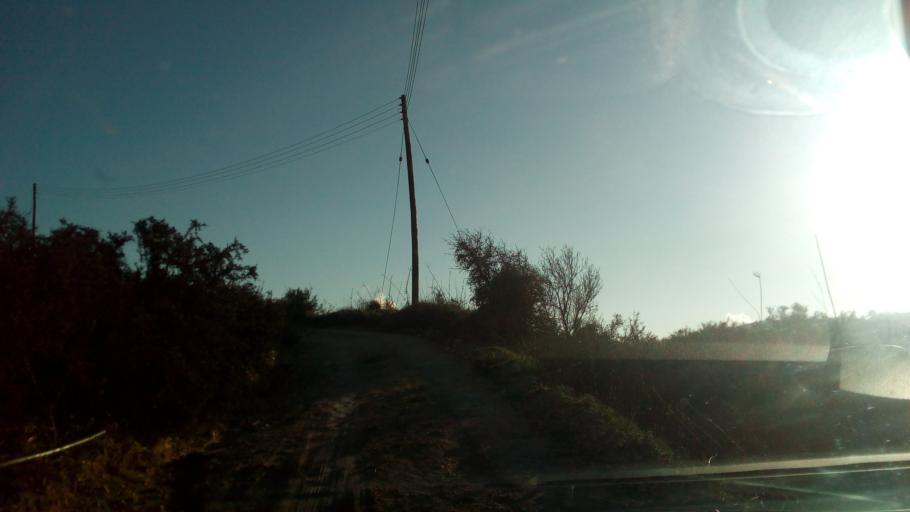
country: CY
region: Pafos
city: Mesogi
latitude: 34.8470
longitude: 32.4861
